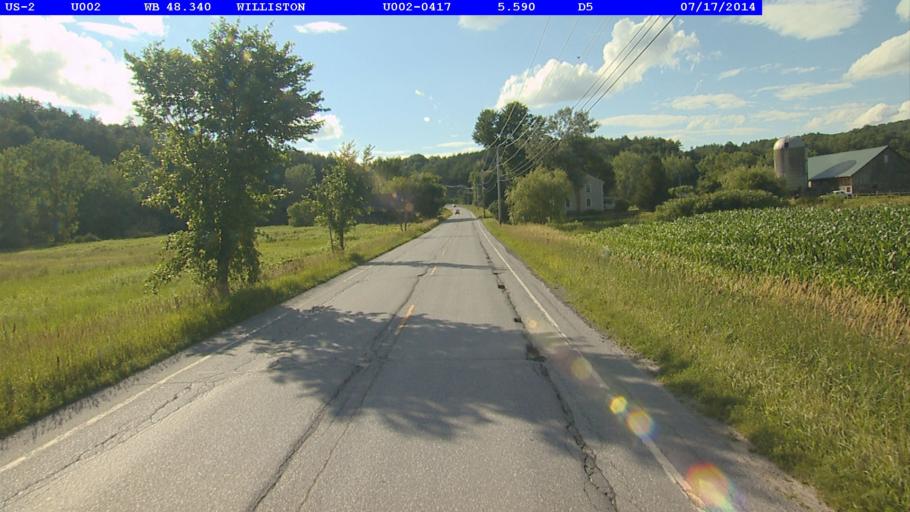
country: US
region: Vermont
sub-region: Chittenden County
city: Williston
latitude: 44.4319
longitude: -73.0332
